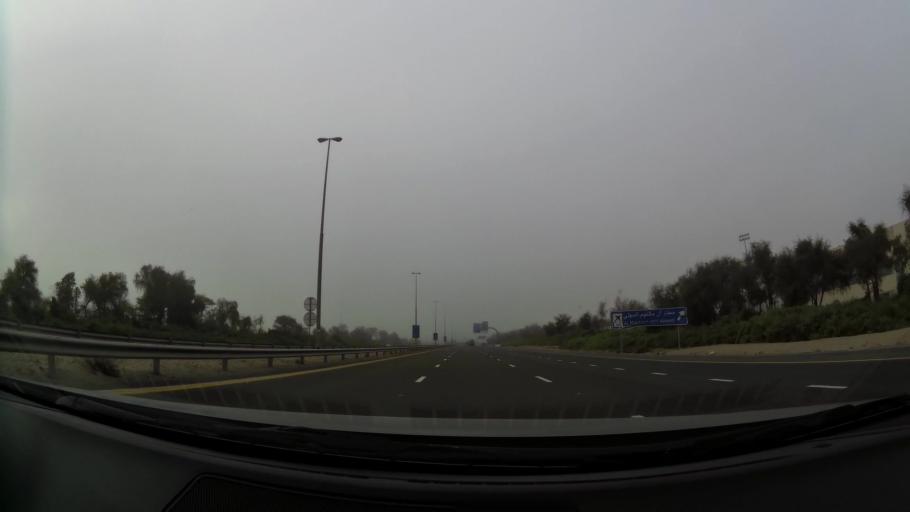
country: AE
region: Dubai
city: Dubai
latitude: 25.1270
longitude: 55.3587
